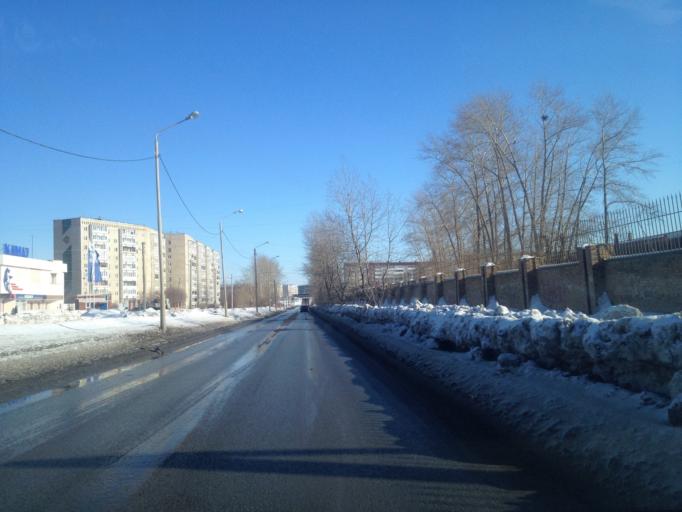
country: RU
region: Sverdlovsk
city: Sovkhoznyy
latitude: 56.7564
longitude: 60.6000
